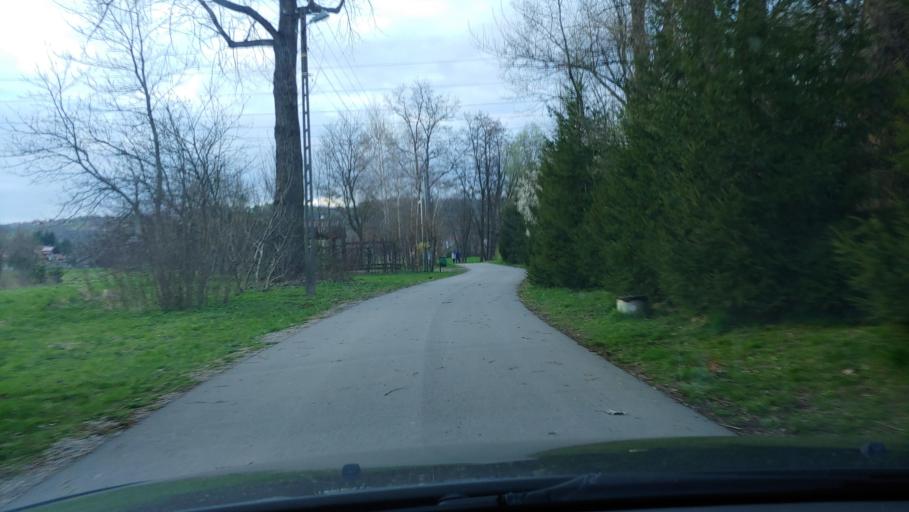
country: PL
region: Lesser Poland Voivodeship
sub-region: Powiat krakowski
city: Bolechowice
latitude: 50.1423
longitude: 19.7914
